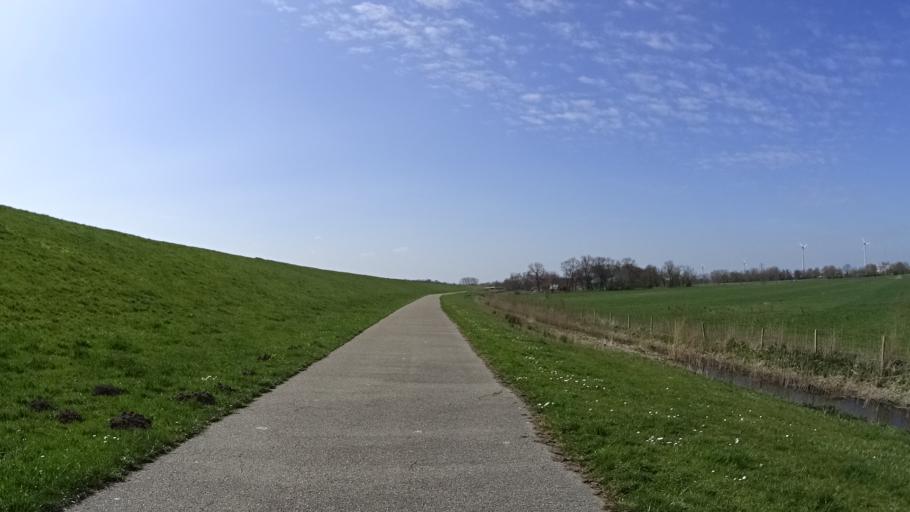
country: DE
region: Lower Saxony
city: Weener
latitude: 53.1773
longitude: 7.3804
